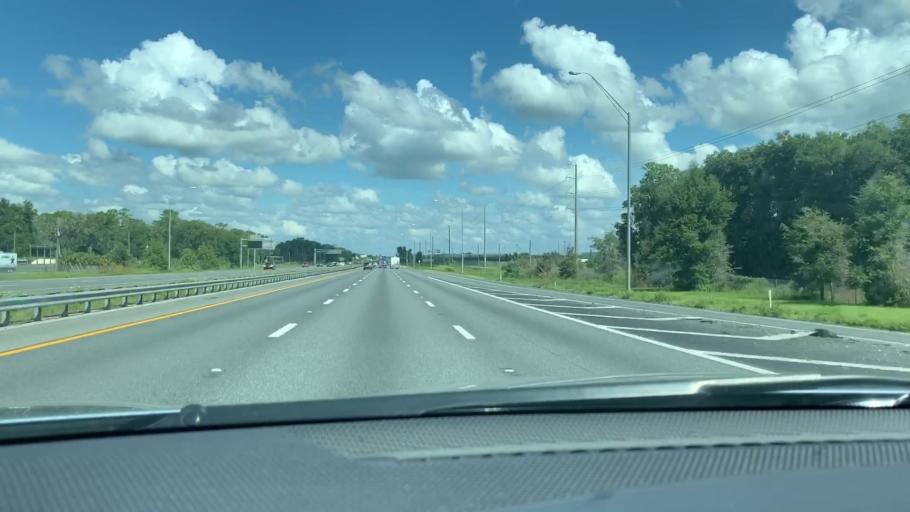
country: US
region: Florida
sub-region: Marion County
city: Ocala
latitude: 29.2104
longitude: -82.1844
